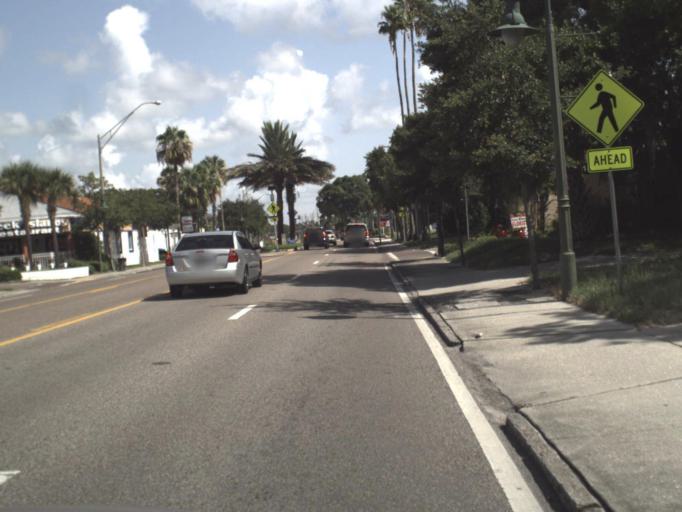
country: US
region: Florida
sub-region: Pinellas County
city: Belleair
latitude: 27.9302
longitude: -82.7957
